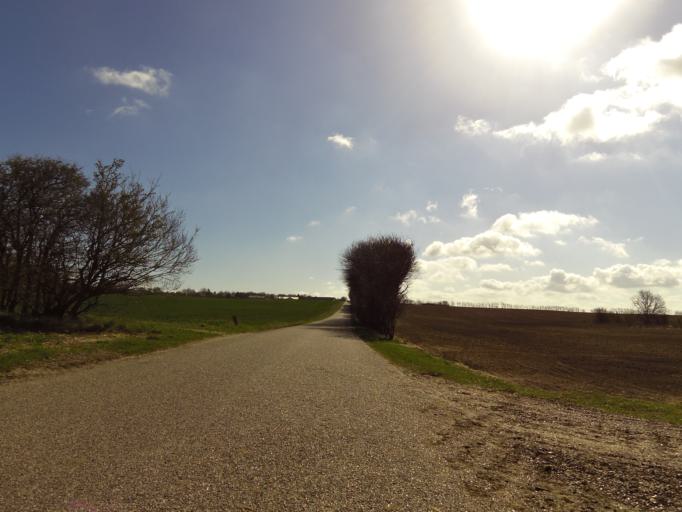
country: DK
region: Central Jutland
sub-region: Holstebro Kommune
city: Vinderup
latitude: 56.4352
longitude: 8.7642
